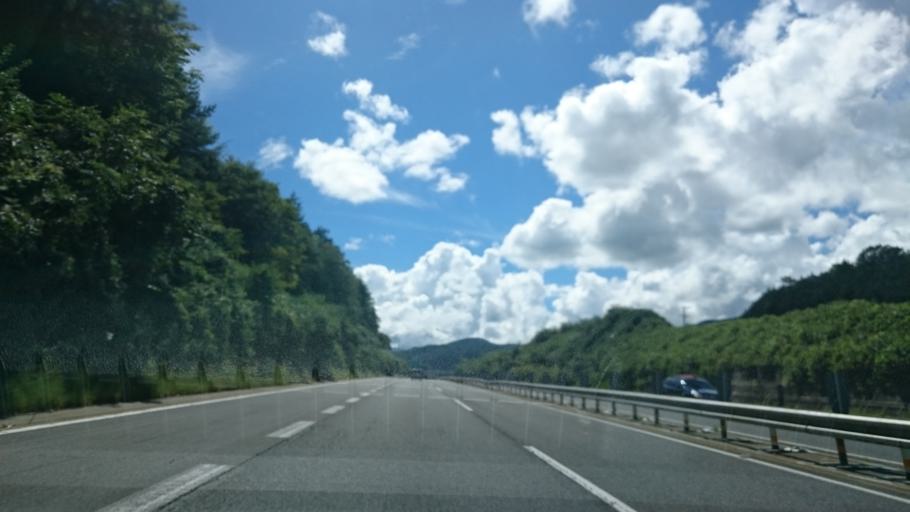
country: JP
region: Nagano
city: Iida
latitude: 35.4847
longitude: 137.7742
